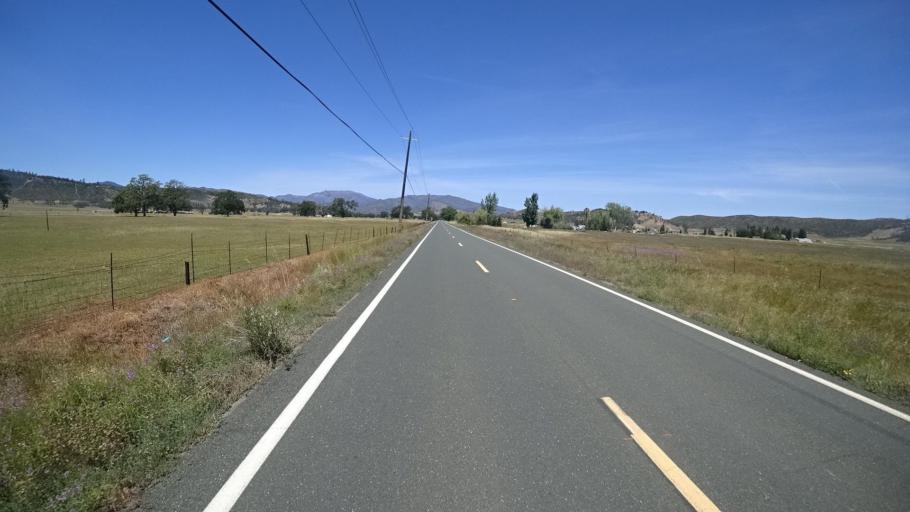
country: US
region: California
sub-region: Lake County
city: Middletown
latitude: 38.7404
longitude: -122.5700
